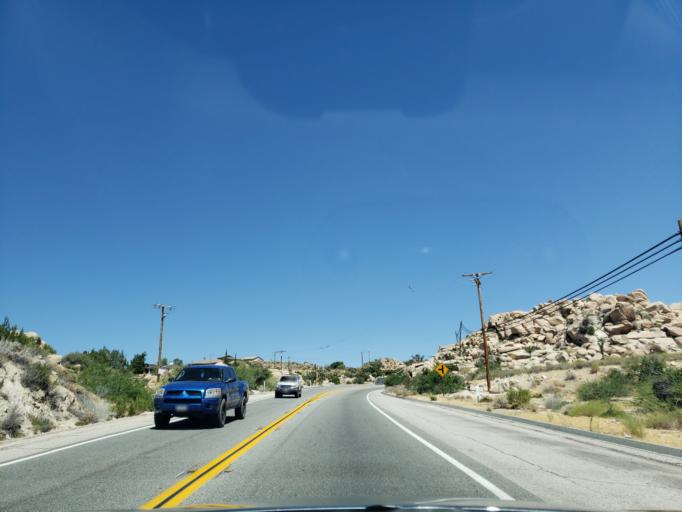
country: US
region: California
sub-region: San Bernardino County
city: Yucca Valley
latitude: 34.1465
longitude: -116.4179
